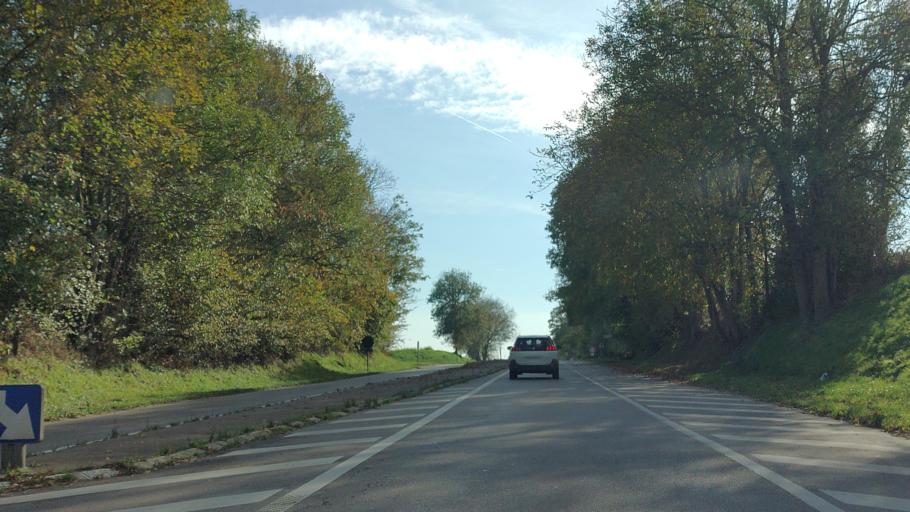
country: FR
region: Ile-de-France
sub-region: Departement du Val-d'Oise
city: Survilliers
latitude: 49.0799
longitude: 2.5293
